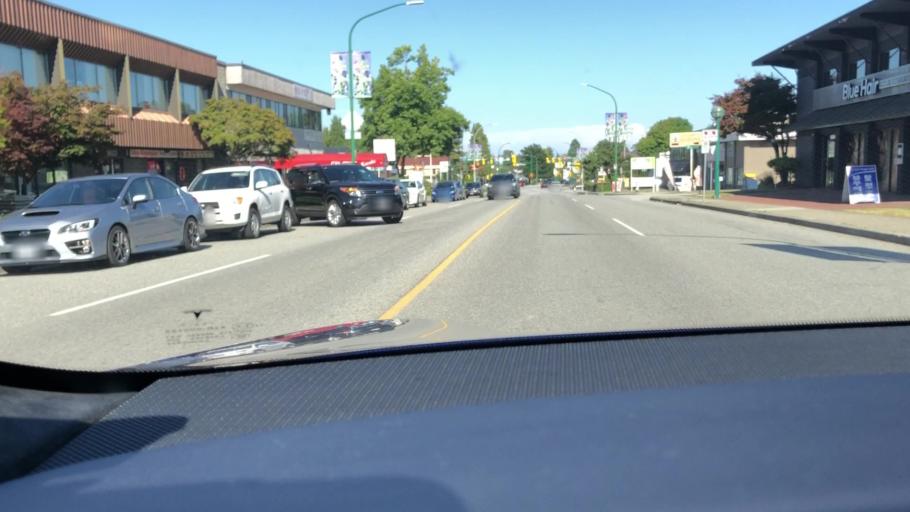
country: CA
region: British Columbia
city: Burnaby
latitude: 49.2219
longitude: -122.9824
